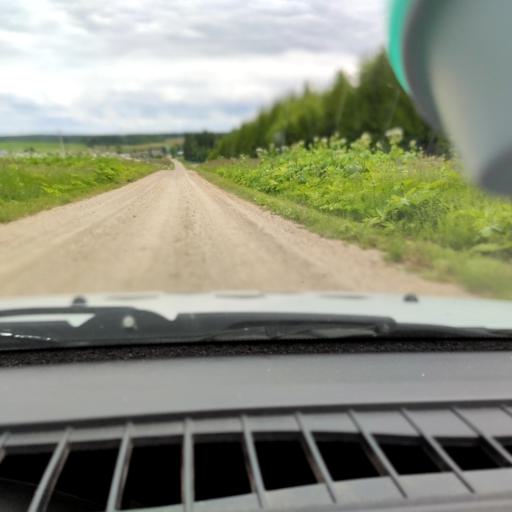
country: RU
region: Perm
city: Suksun
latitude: 57.2136
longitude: 57.6845
